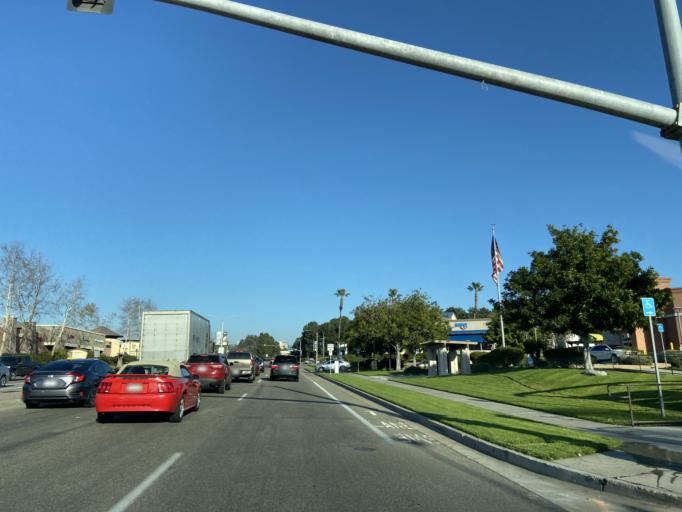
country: US
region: California
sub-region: San Diego County
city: Bonita
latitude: 32.6474
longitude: -116.9673
